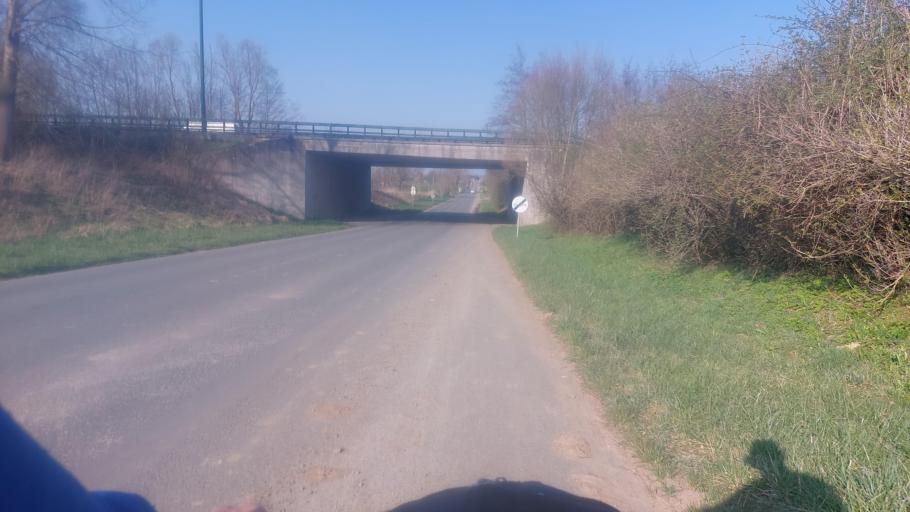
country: BE
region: Wallonia
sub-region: Province du Hainaut
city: Lessines
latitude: 50.6745
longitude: 3.8368
